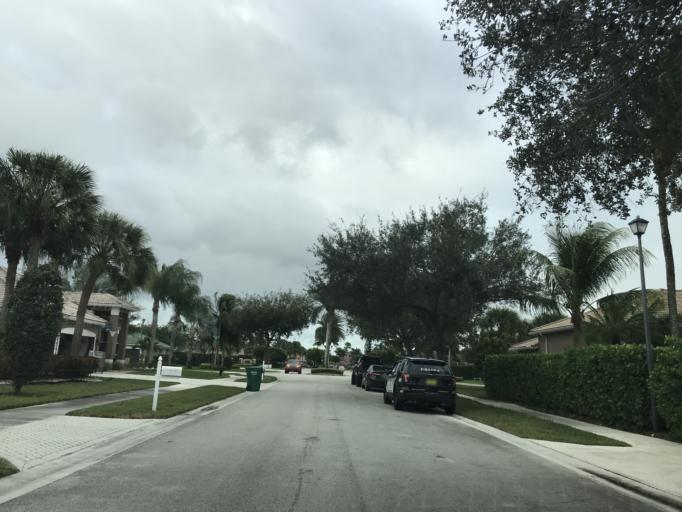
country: US
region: Florida
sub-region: Broward County
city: Coral Springs
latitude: 26.2992
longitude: -80.2753
